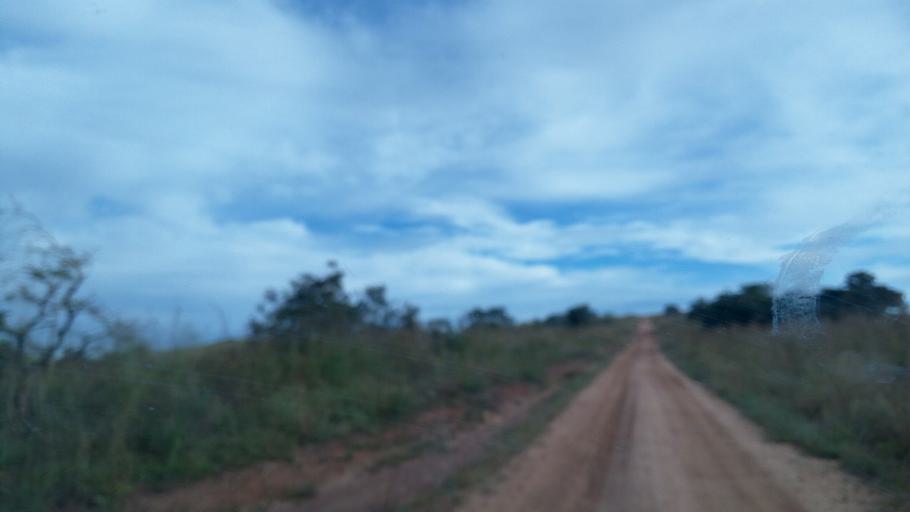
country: CD
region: Katanga
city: Kalemie
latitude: -6.3503
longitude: 29.0477
